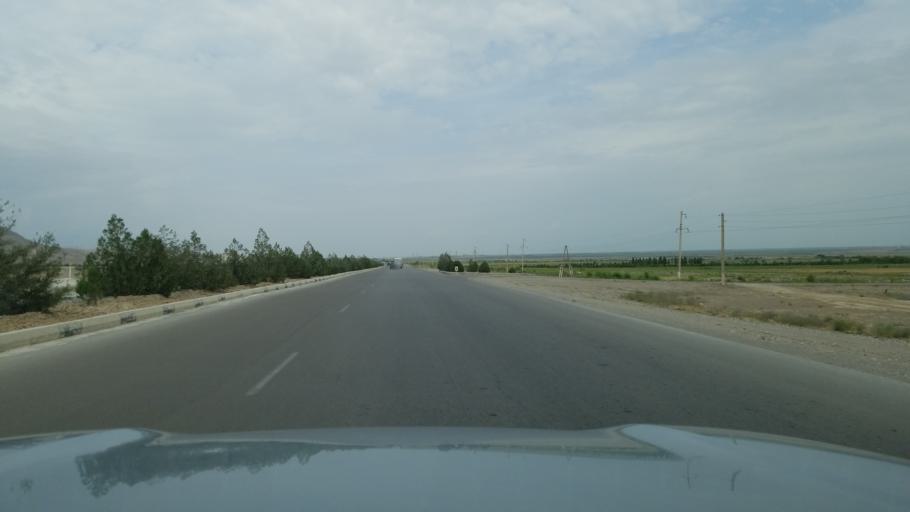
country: TM
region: Ahal
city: Baharly
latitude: 38.2334
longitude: 57.7806
